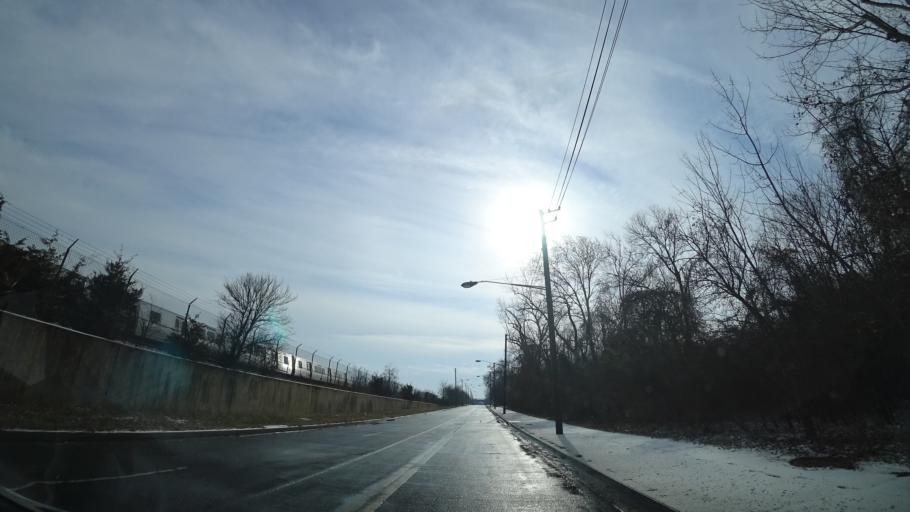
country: US
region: Maryland
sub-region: Prince George's County
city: Chillum
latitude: 38.9455
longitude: -76.9998
